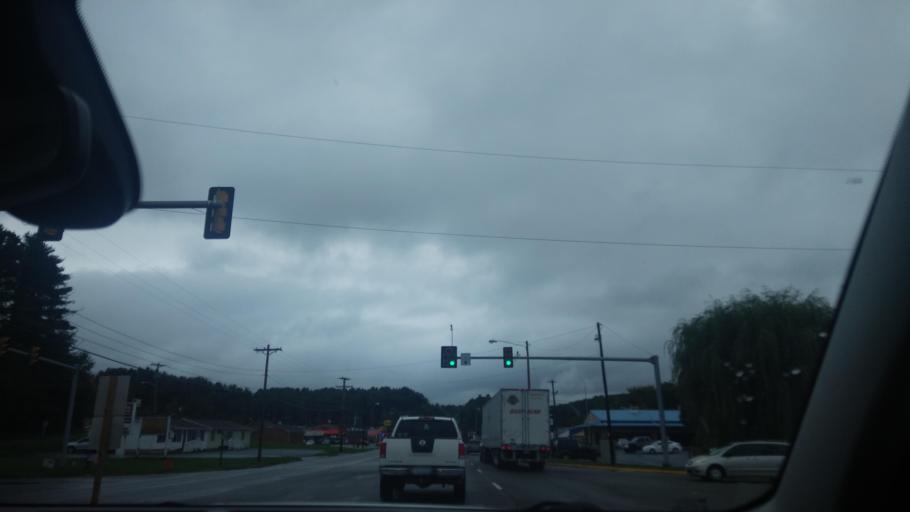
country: US
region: Virginia
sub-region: City of Galax
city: Galax
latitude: 36.6819
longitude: -80.8935
